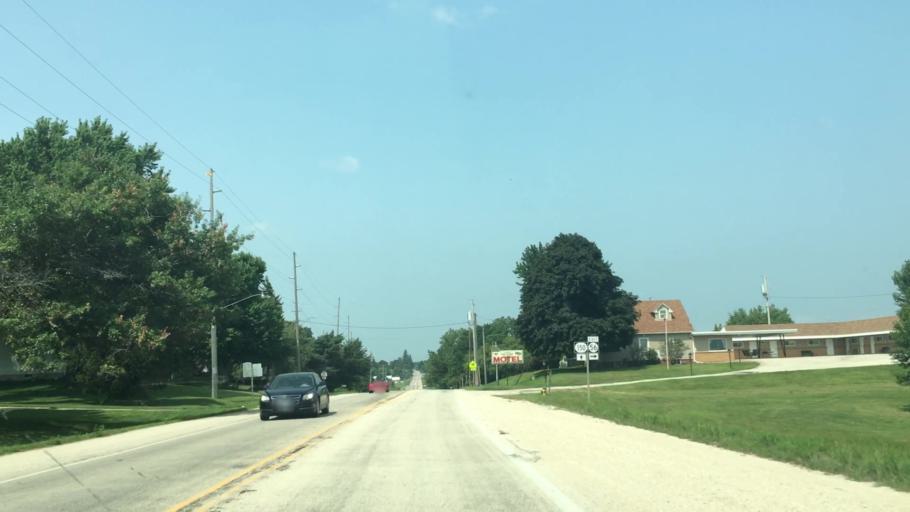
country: US
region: Iowa
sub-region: Fayette County
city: West Union
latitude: 42.9496
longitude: -91.8142
